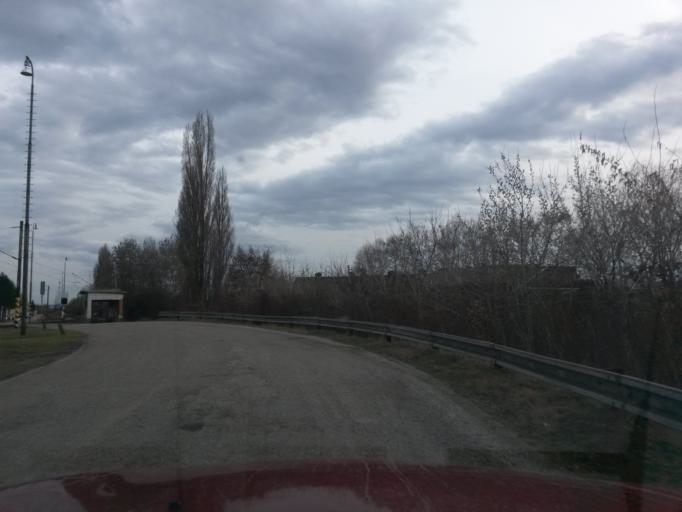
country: SK
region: Kosicky
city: Kosice
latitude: 48.7156
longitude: 21.2709
